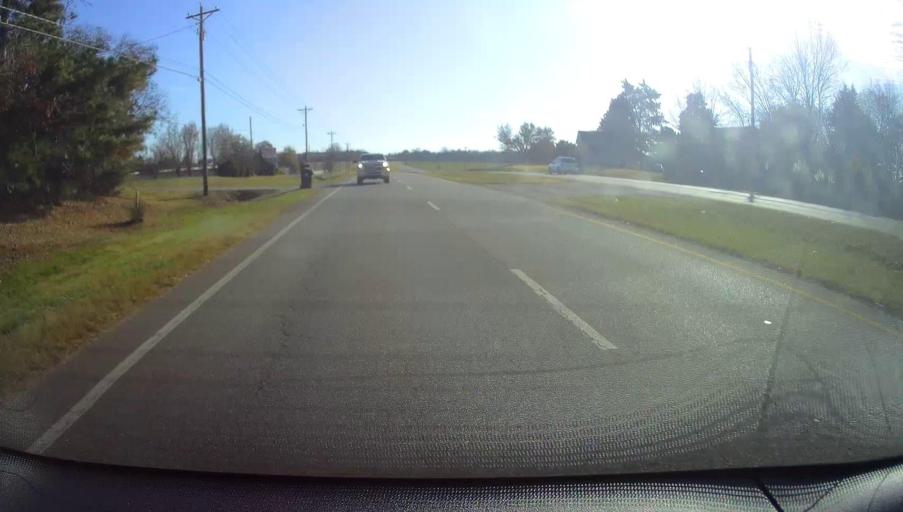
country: US
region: Alabama
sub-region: Limestone County
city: Athens
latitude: 34.7479
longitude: -86.9570
